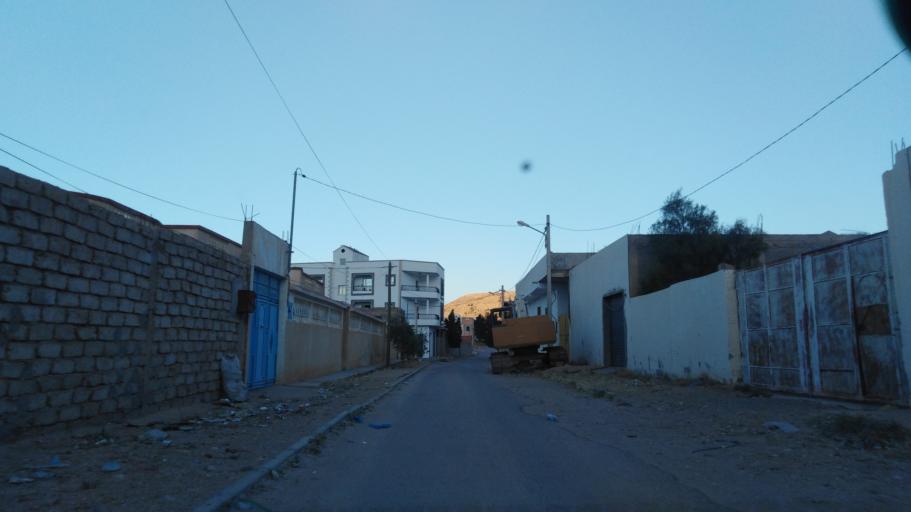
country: TN
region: Tataouine
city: Tataouine
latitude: 32.9421
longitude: 10.4537
